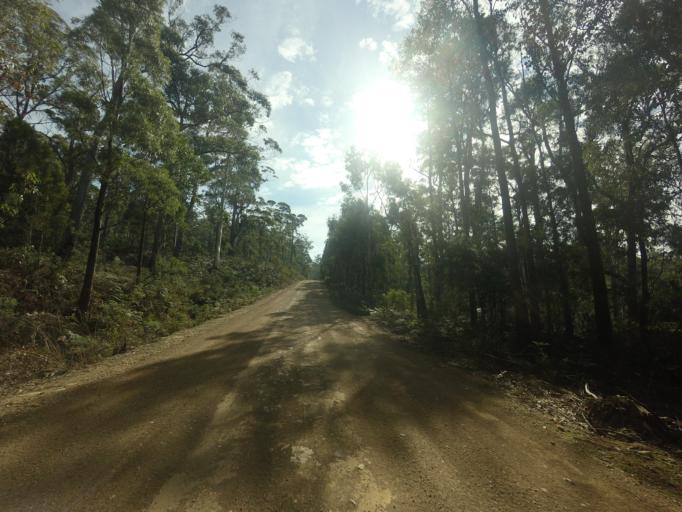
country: AU
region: Tasmania
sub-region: Sorell
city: Sorell
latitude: -42.5573
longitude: 147.4594
